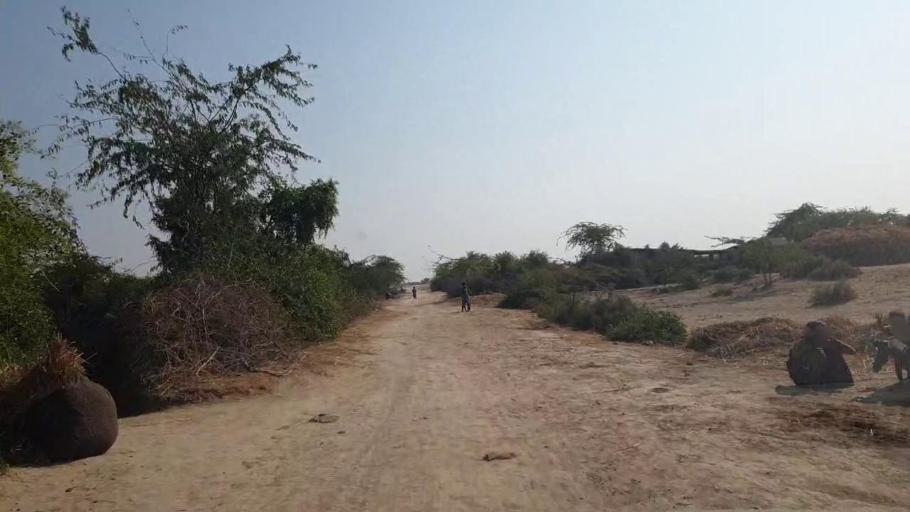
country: PK
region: Sindh
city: Matli
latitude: 24.9677
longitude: 68.6464
